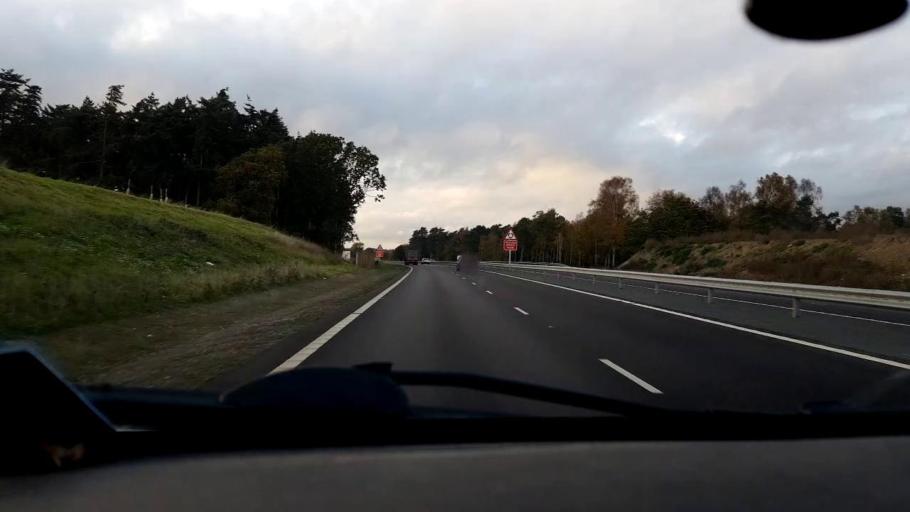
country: GB
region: England
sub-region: Norfolk
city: Horsford
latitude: 52.6952
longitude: 1.2192
